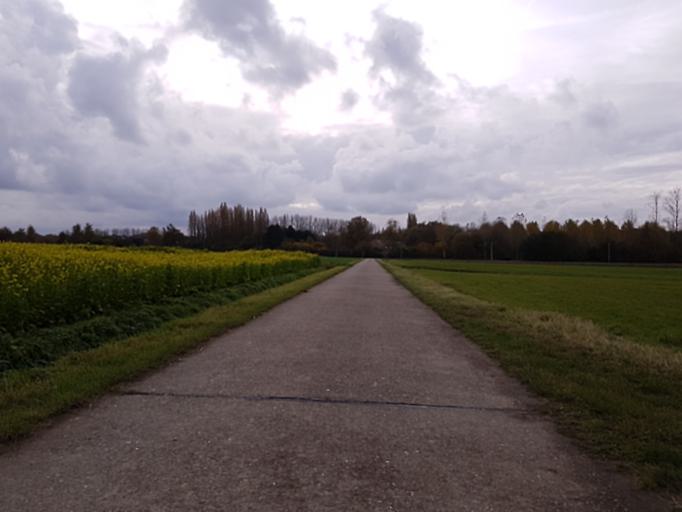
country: BE
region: Flanders
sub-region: Provincie Antwerpen
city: Boechout
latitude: 51.1548
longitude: 4.5047
